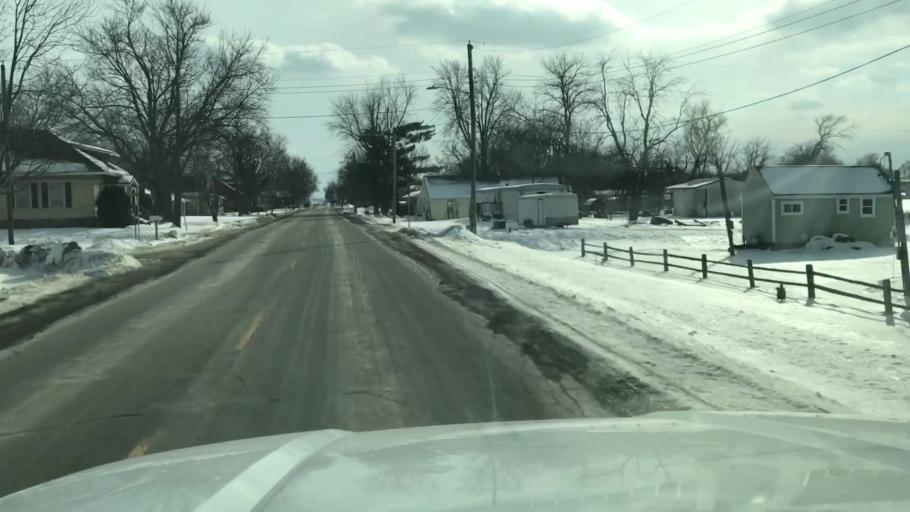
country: US
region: Missouri
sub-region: Gentry County
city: Stanberry
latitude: 40.3560
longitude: -94.6731
